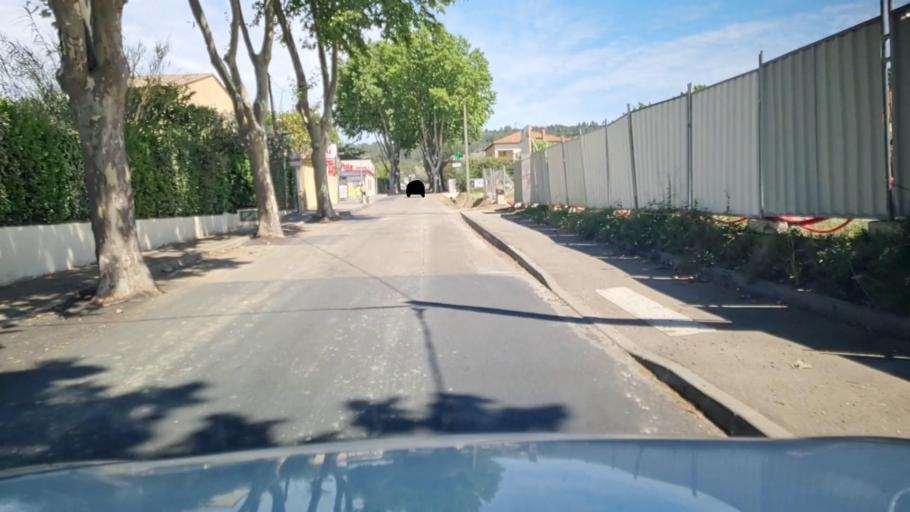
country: FR
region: Languedoc-Roussillon
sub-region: Departement du Gard
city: Clarensac
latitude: 43.8263
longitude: 4.2247
